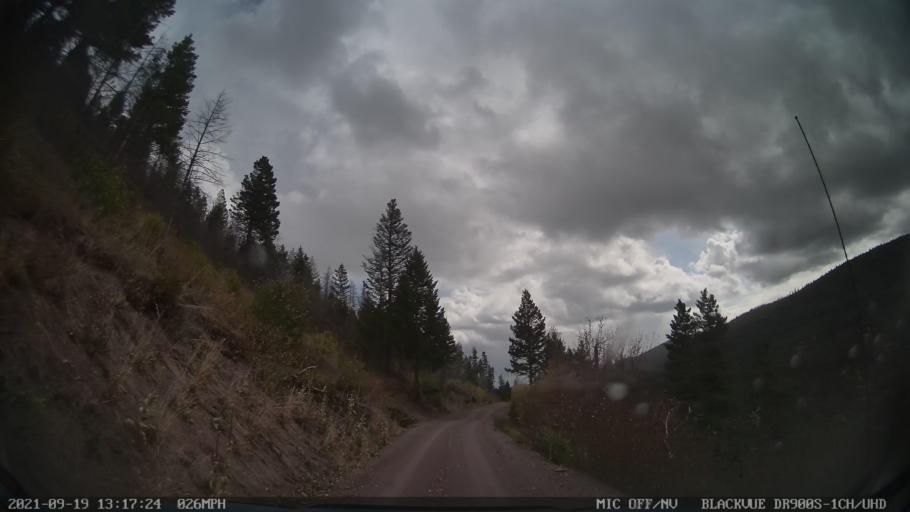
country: US
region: Montana
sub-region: Missoula County
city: Seeley Lake
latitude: 47.1748
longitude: -113.3636
